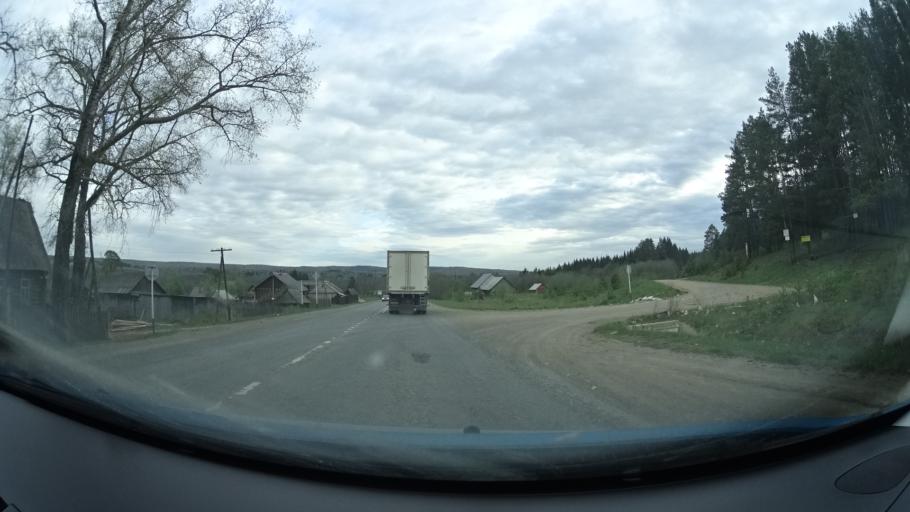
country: RU
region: Perm
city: Yugo-Kamskiy
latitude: 57.5504
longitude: 55.6851
